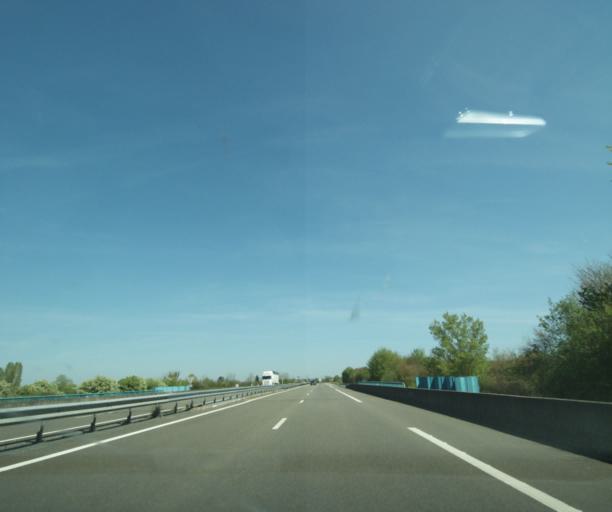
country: FR
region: Bourgogne
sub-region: Departement de la Nievre
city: Saint-Eloi
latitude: 46.9782
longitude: 3.2008
